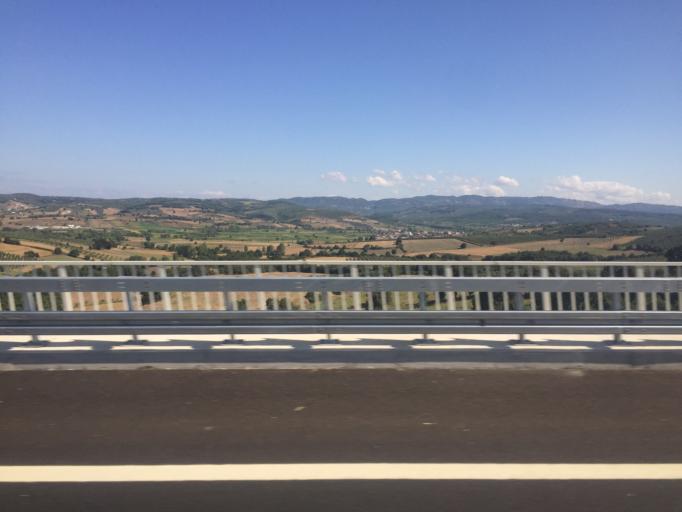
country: TR
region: Bursa
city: Gorukle
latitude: 40.2559
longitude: 28.7348
